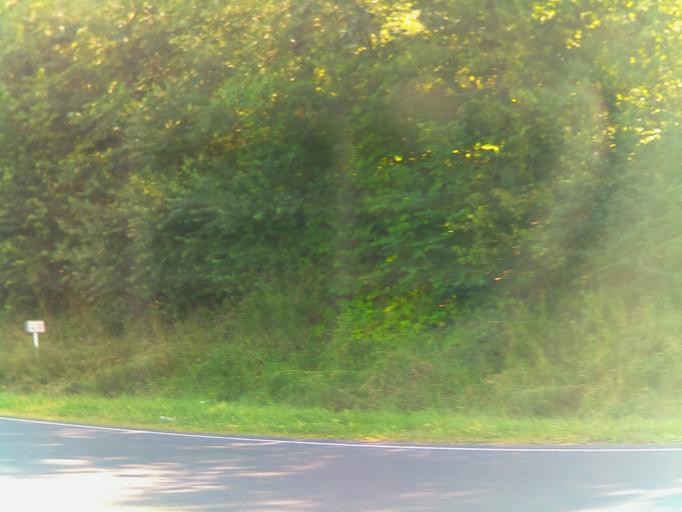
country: DE
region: Bavaria
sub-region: Regierungsbezirk Unterfranken
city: Riedenberg
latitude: 50.3153
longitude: 9.8375
